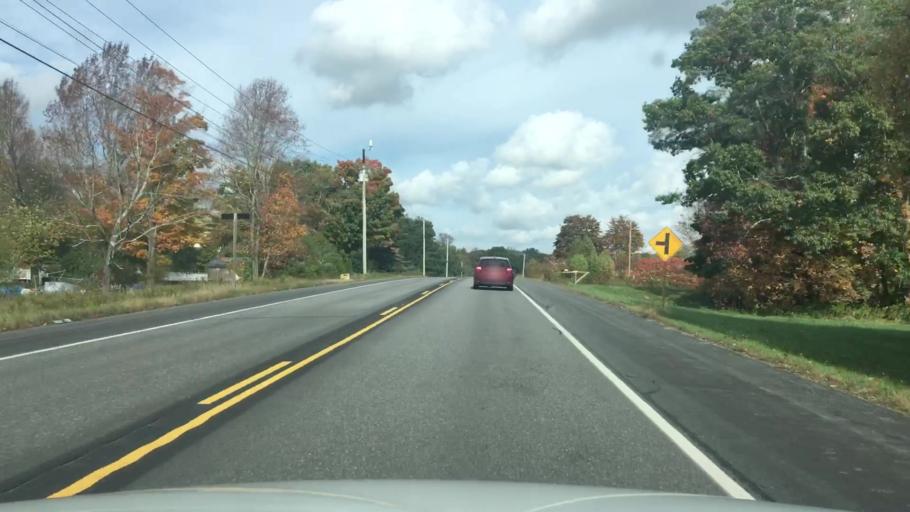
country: US
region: Maine
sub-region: Knox County
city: Rockport
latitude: 44.1584
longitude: -69.1159
